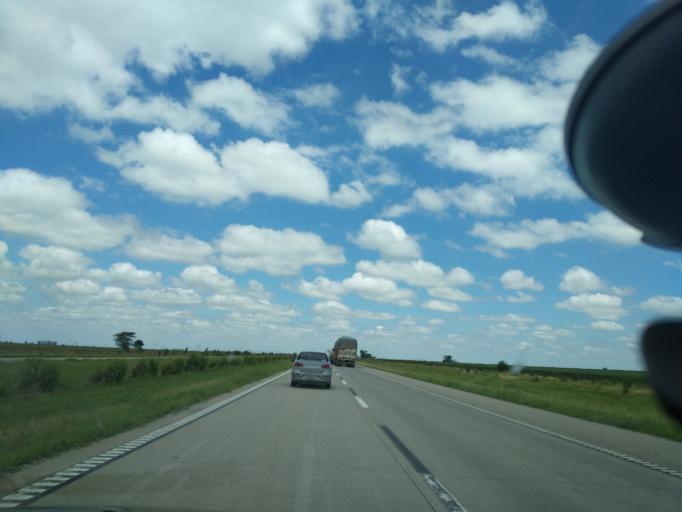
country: AR
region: Cordoba
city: Tio Pujio
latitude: -32.2870
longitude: -63.3015
